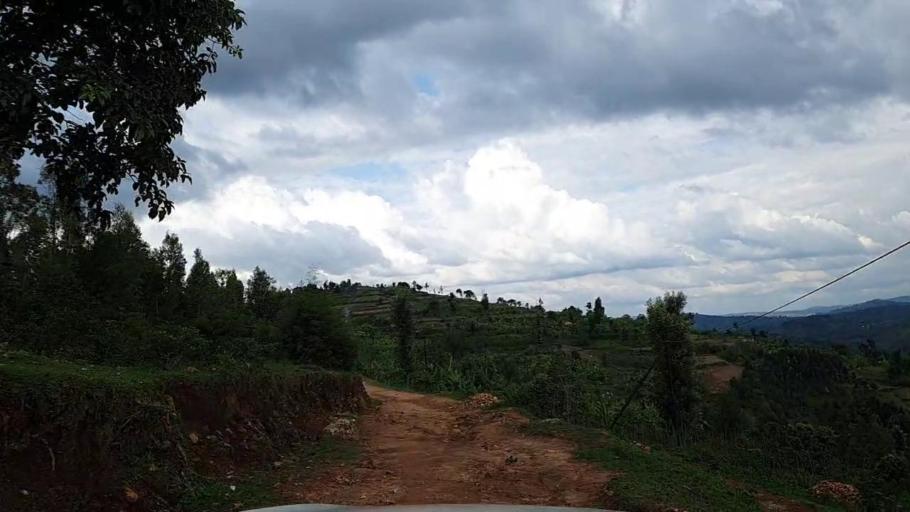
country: RW
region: Southern Province
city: Gikongoro
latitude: -2.4345
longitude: 29.6373
